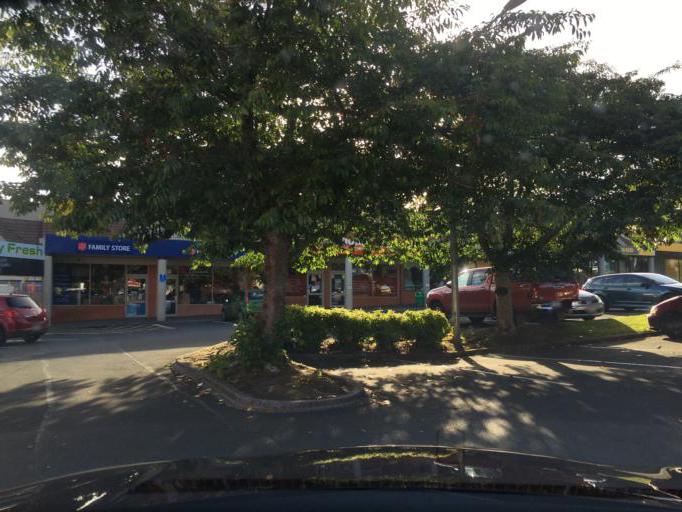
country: NZ
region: Waikato
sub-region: Waipa District
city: Cambridge
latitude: -38.0110
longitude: 175.3274
